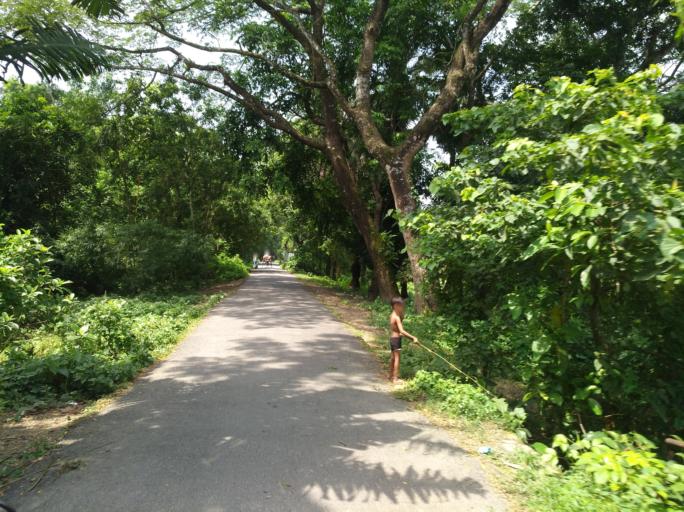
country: BD
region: Dhaka
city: Palang
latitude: 23.2522
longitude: 90.3106
